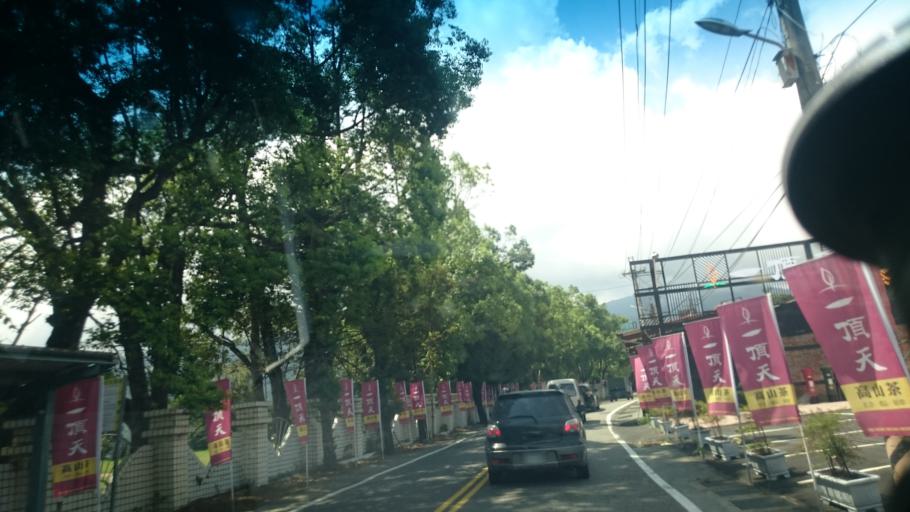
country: TW
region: Taiwan
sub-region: Nantou
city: Puli
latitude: 24.0322
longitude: 121.1422
